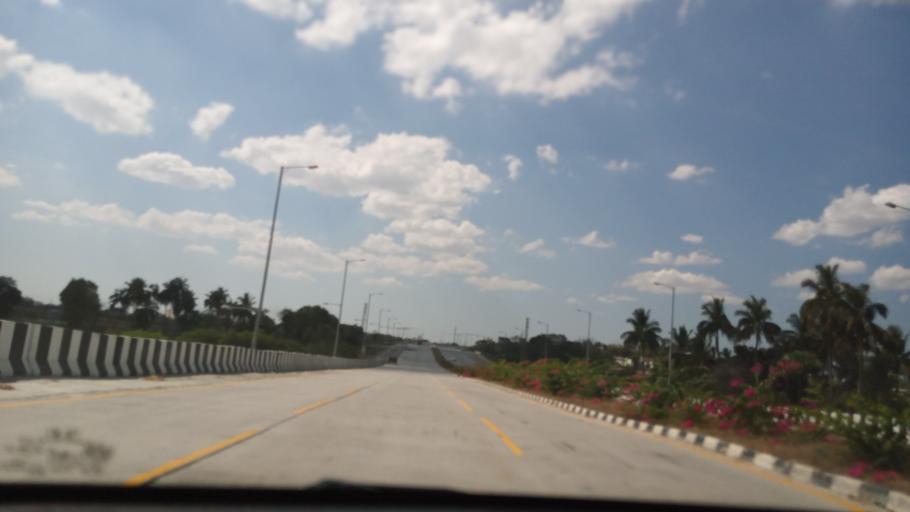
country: IN
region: Andhra Pradesh
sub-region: Chittoor
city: Palmaner
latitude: 13.2136
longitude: 78.7491
